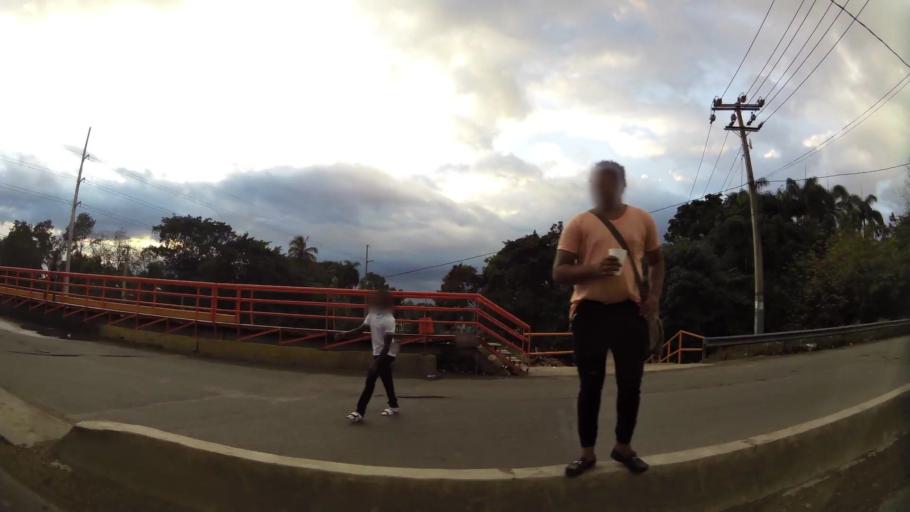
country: DO
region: Santo Domingo
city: Santo Domingo Oeste
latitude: 18.5031
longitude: -69.9987
